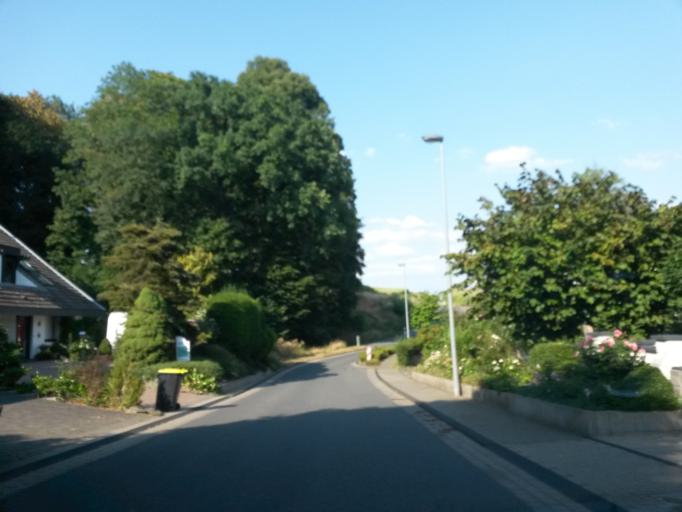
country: DE
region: North Rhine-Westphalia
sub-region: Regierungsbezirk Koln
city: Rosrath
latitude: 50.8923
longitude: 7.2115
